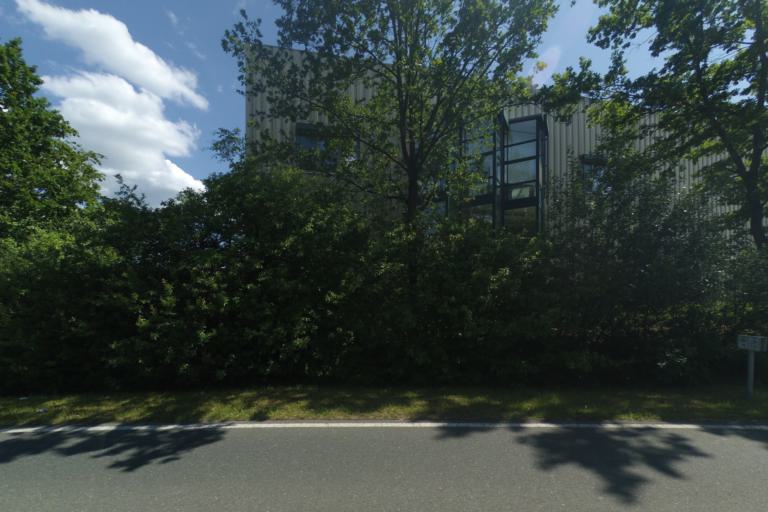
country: DE
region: Bavaria
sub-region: Regierungsbezirk Mittelfranken
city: Adelsdorf
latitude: 49.7114
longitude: 10.8848
